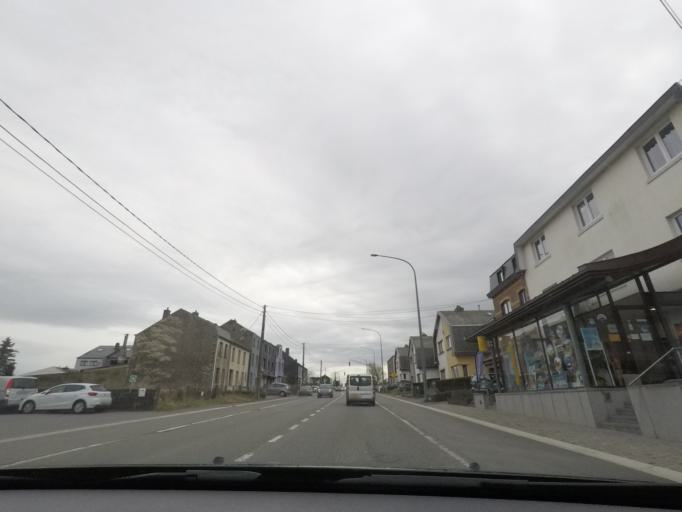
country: BE
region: Wallonia
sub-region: Province du Luxembourg
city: Bastogne
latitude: 49.9960
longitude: 5.7226
